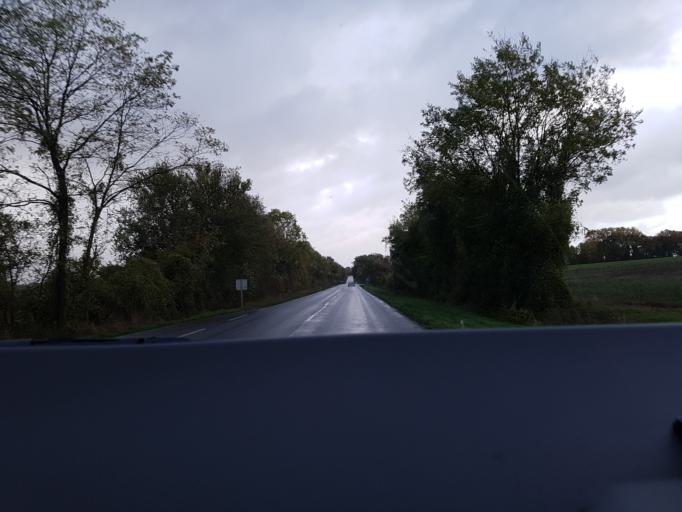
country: FR
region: Poitou-Charentes
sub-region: Departement des Deux-Sevres
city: Melle
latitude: 46.1982
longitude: -0.1653
